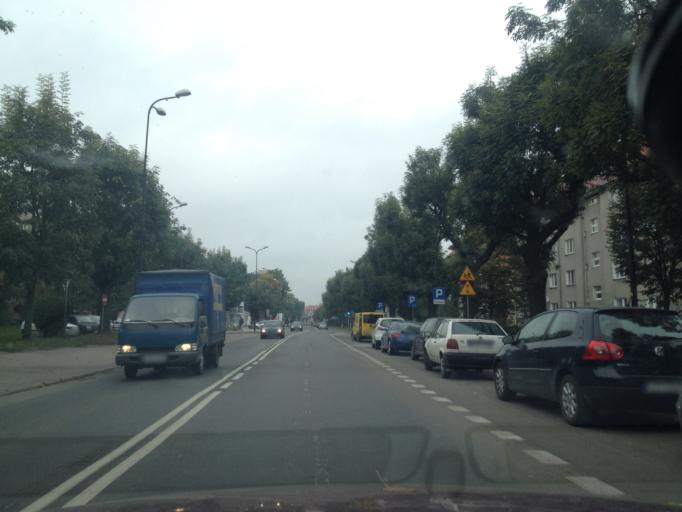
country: PL
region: Lower Silesian Voivodeship
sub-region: Powiat zgorzelecki
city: Zgorzelec
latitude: 51.1434
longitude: 15.0102
